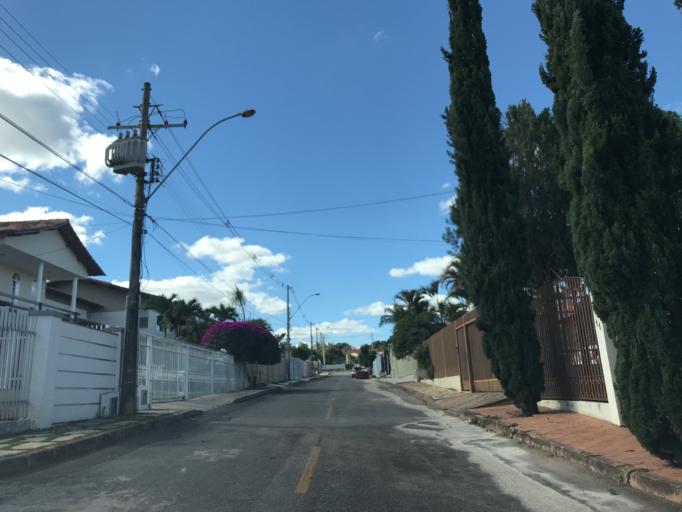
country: BR
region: Federal District
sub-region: Brasilia
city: Brasilia
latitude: -15.7593
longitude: -47.8423
